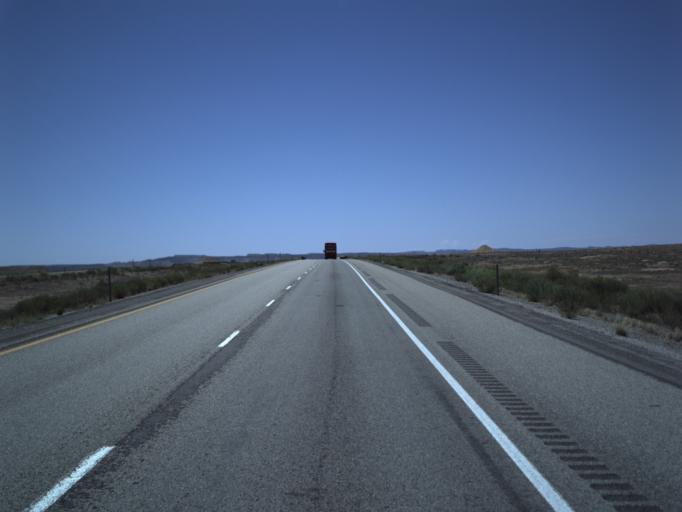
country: US
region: Utah
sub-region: Grand County
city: Moab
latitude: 38.9575
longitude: -109.3847
